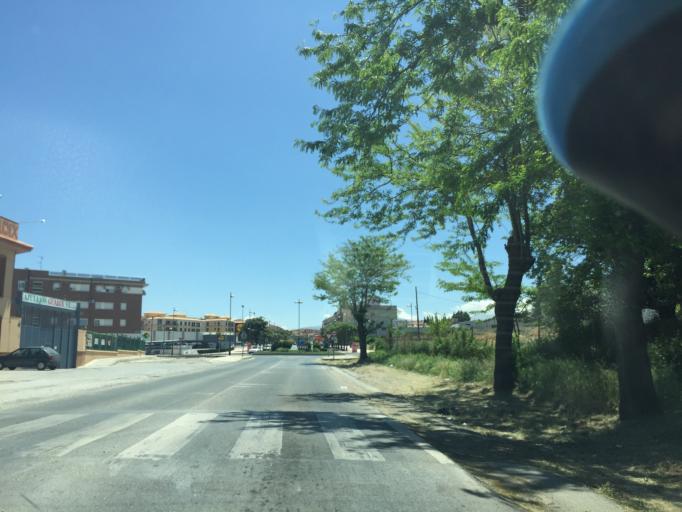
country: ES
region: Andalusia
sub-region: Provincia de Granada
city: Guadix
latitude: 37.3080
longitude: -3.1459
